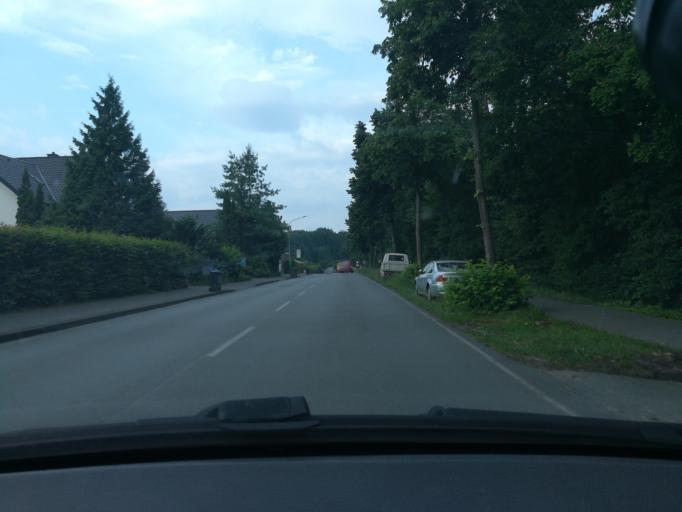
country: DE
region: North Rhine-Westphalia
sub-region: Regierungsbezirk Detmold
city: Oerlinghausen
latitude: 51.9148
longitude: 8.6552
